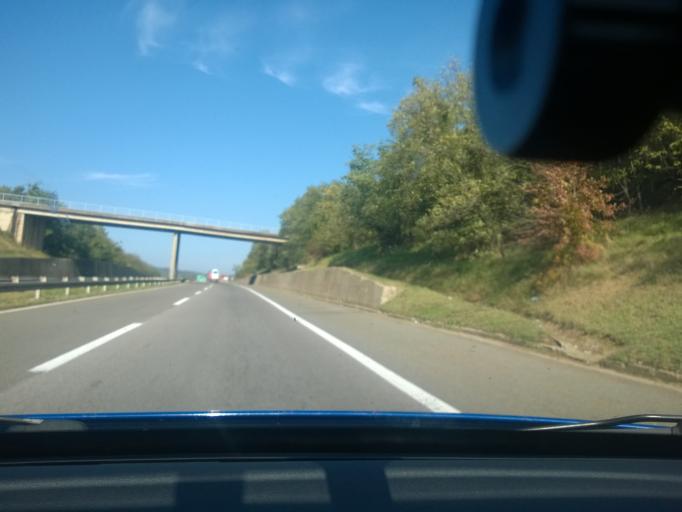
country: RS
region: Central Serbia
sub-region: Nisavski Okrug
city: Razanj
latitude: 43.6672
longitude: 21.5484
